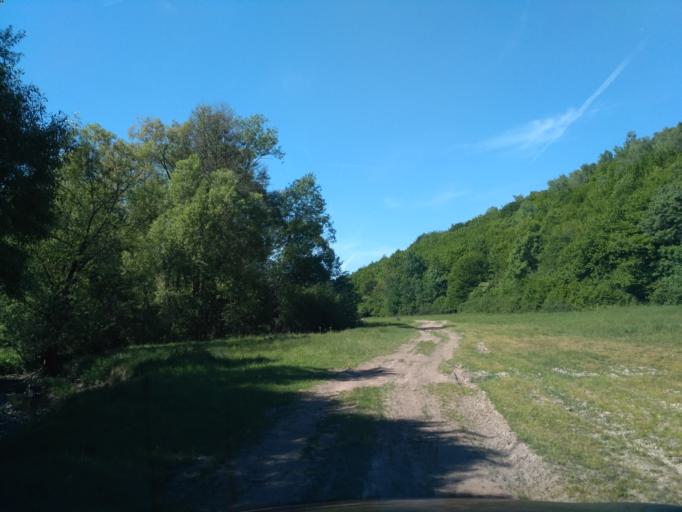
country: SK
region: Presovsky
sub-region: Okres Presov
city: Presov
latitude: 48.8869
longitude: 21.3942
